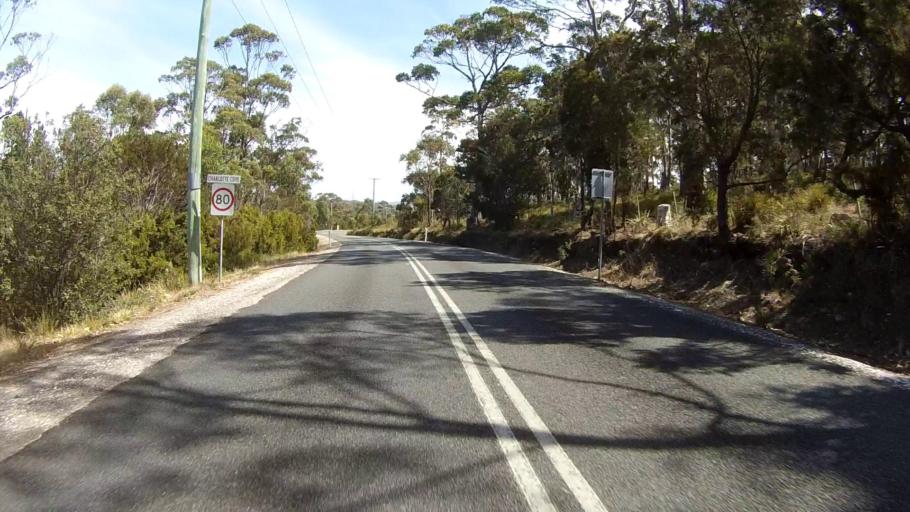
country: AU
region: Tasmania
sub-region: Huon Valley
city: Cygnet
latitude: -43.2724
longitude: 147.1491
